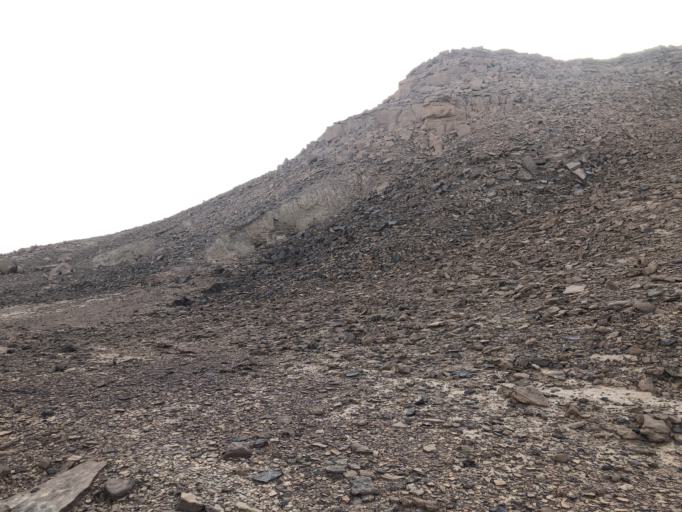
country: SA
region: Ar Riyad
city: shokhaib
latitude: 23.6288
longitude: 46.0844
